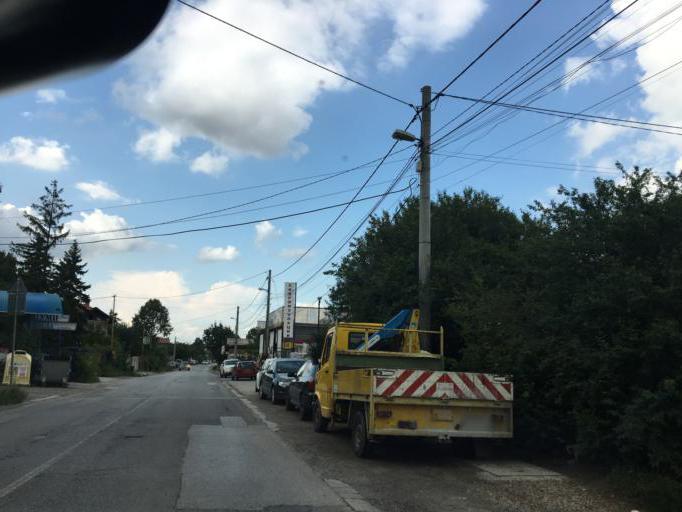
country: BG
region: Sofia-Capital
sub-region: Stolichna Obshtina
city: Sofia
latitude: 42.6349
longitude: 23.3539
